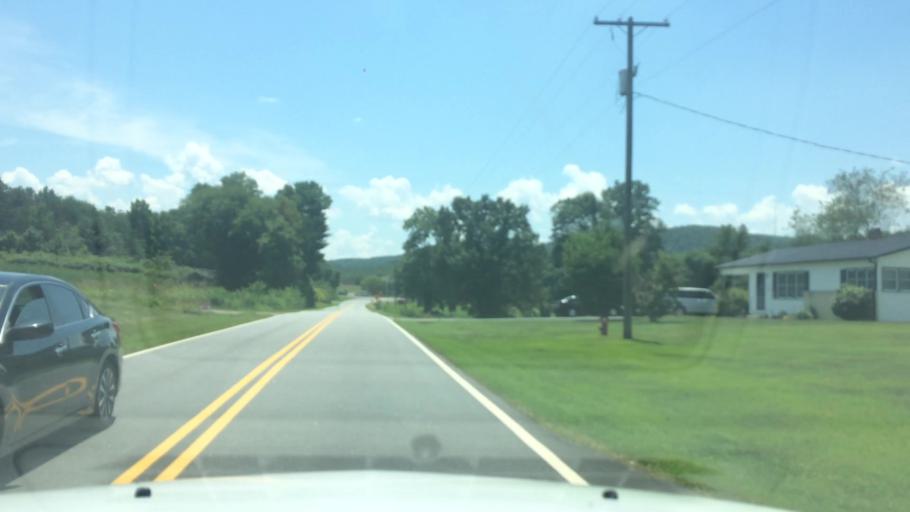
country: US
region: North Carolina
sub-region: Alexander County
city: Taylorsville
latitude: 35.9262
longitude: -81.2621
